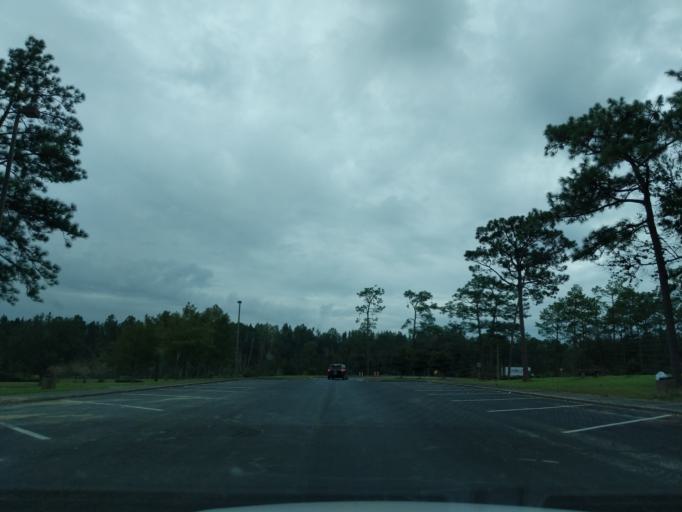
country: US
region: Florida
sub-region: Escambia County
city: Cantonment
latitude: 30.5784
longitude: -87.4225
